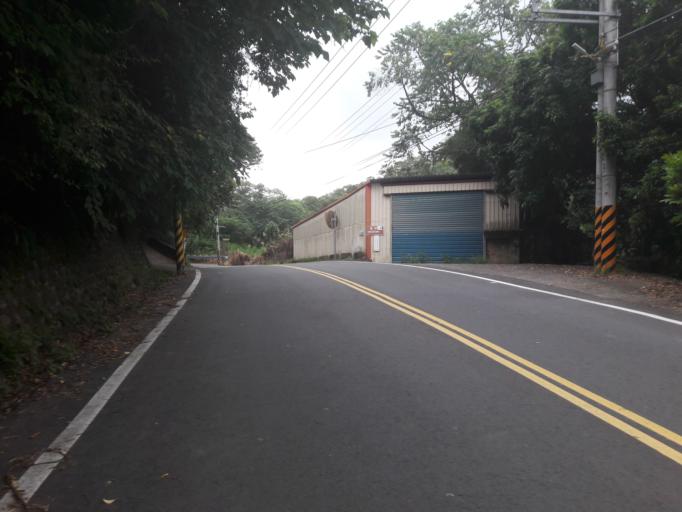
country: TW
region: Taiwan
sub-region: Hsinchu
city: Hsinchu
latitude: 24.7295
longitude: 120.9685
